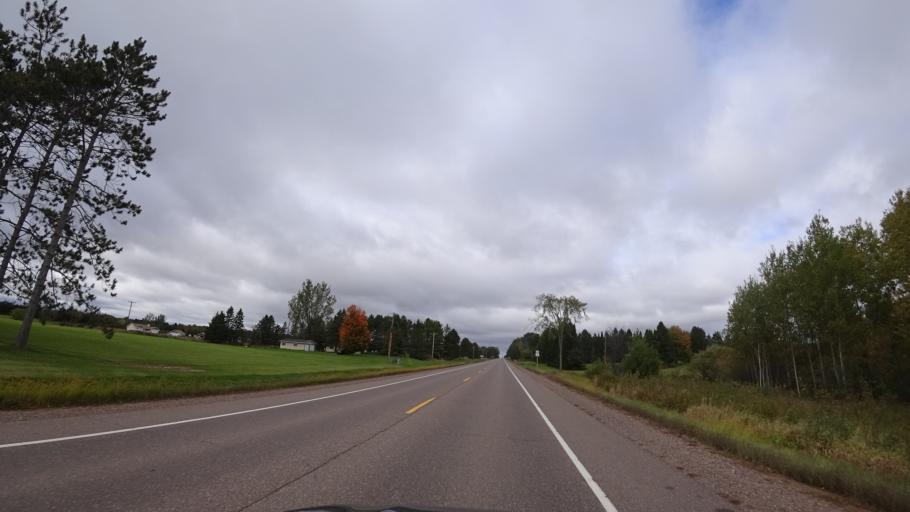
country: US
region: Wisconsin
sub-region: Rusk County
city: Ladysmith
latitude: 45.5044
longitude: -91.1115
